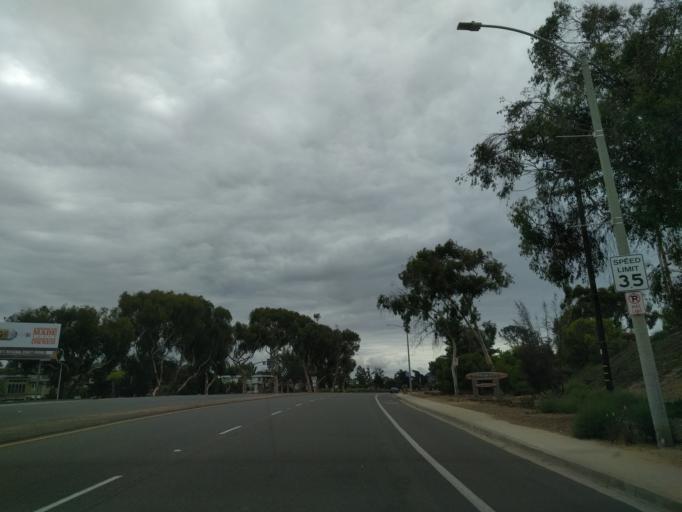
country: US
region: California
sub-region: San Diego County
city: Encinitas
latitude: 33.0821
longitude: -117.3086
